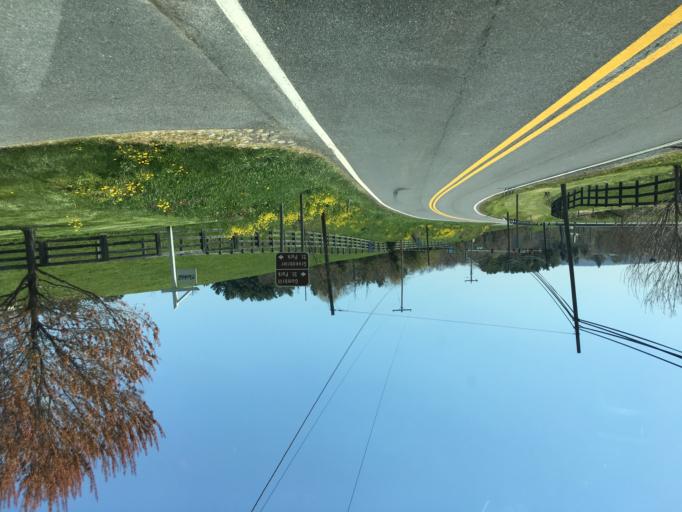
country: US
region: Maryland
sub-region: Frederick County
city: Myersville
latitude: 39.5101
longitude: -77.5577
